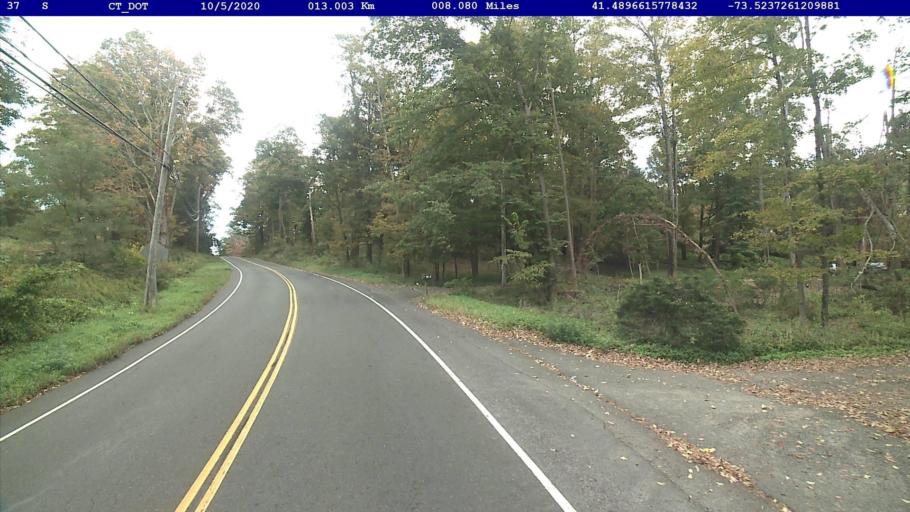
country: US
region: New York
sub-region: Putnam County
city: Putnam Lake
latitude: 41.4911
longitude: -73.5222
